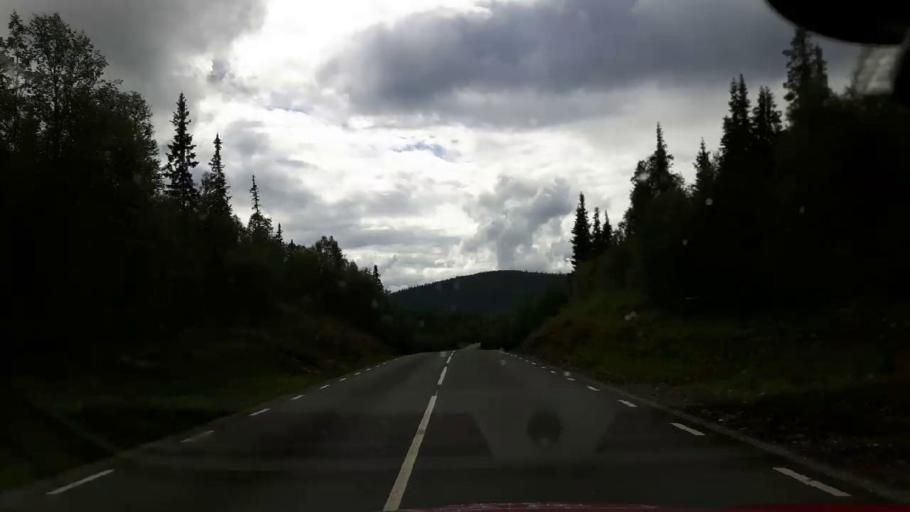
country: NO
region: Nord-Trondelag
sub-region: Royrvik
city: Royrvik
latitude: 64.8976
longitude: 14.1911
